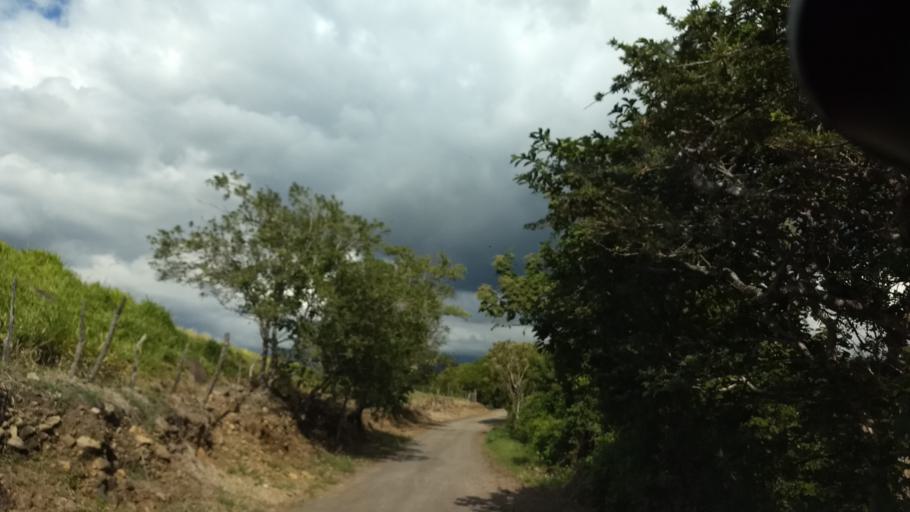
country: MX
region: Colima
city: Suchitlan
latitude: 19.4567
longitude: -103.7679
